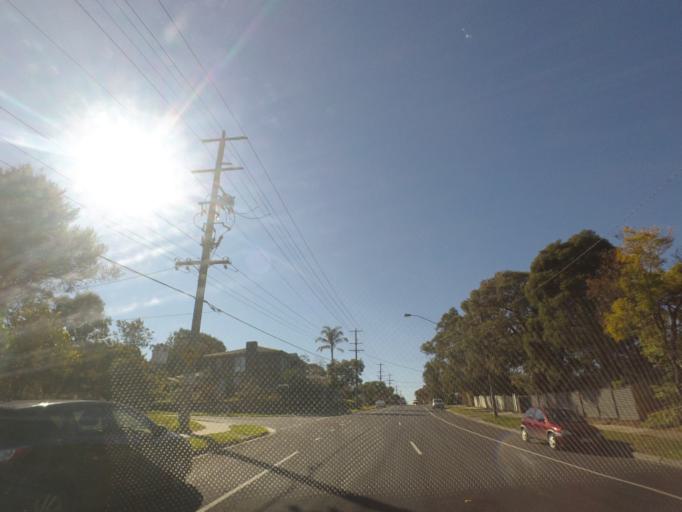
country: AU
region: Victoria
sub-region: Maroondah
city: Croydon Hills
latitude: -37.7890
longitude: 145.2549
